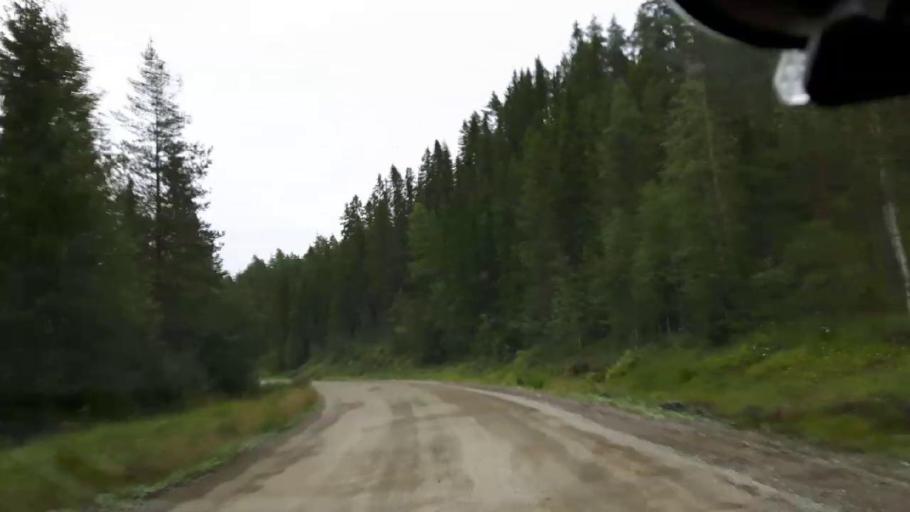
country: SE
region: Vaesternorrland
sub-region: Ange Kommun
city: Ange
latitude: 62.7720
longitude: 15.9220
